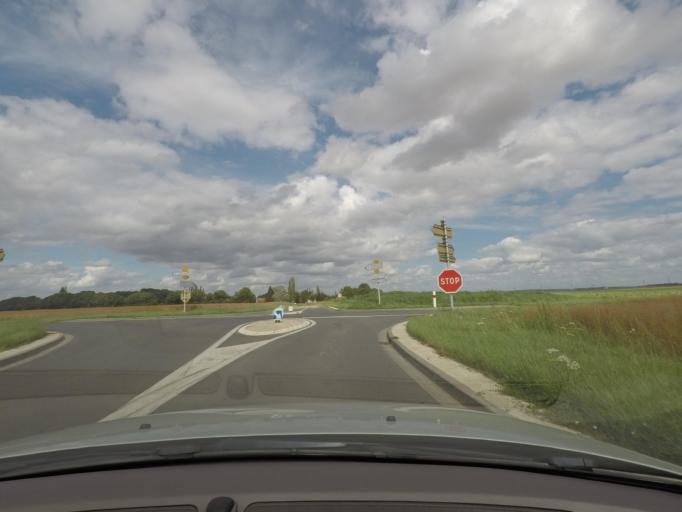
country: FR
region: Haute-Normandie
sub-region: Departement de l'Eure
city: Les Andelys
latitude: 49.2006
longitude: 1.4718
